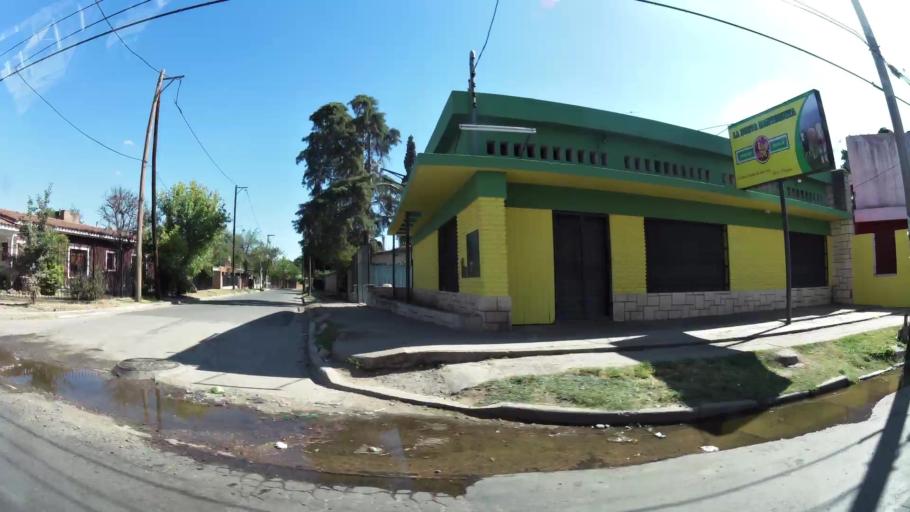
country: AR
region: Cordoba
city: Villa Allende
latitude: -31.3310
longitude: -64.2644
